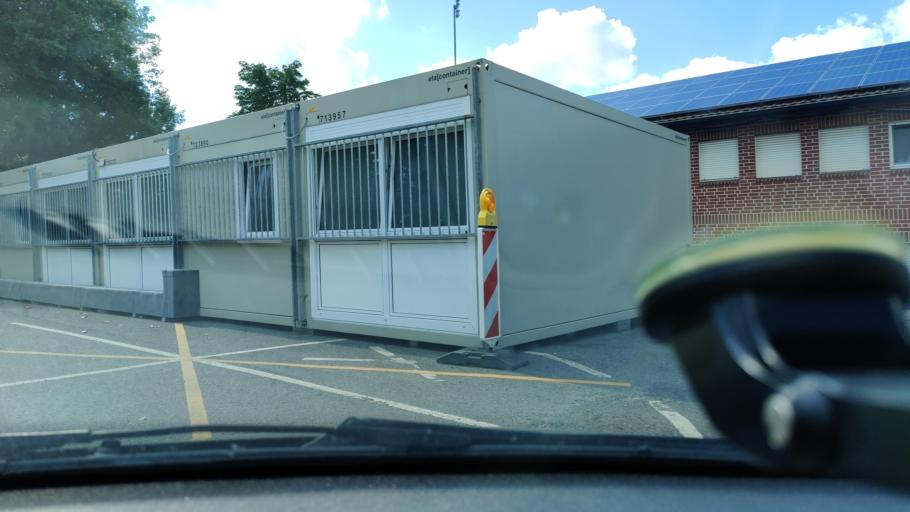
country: DE
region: North Rhine-Westphalia
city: Stadtlohn
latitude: 51.9998
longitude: 6.9287
